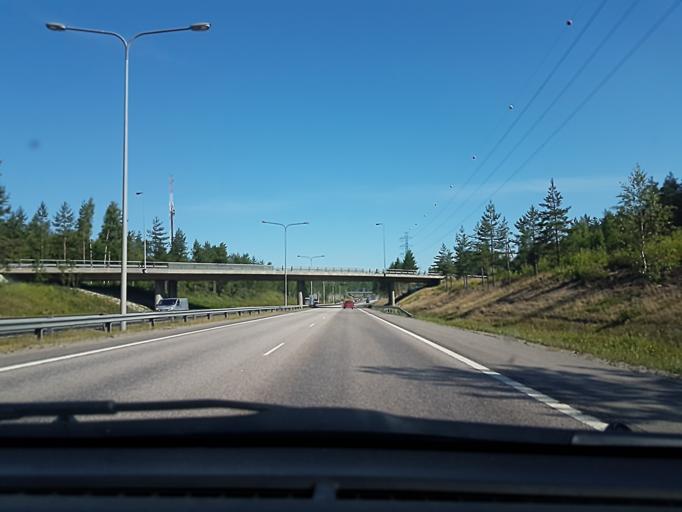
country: FI
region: Uusimaa
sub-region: Helsinki
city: Vantaa
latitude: 60.3165
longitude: 24.9975
